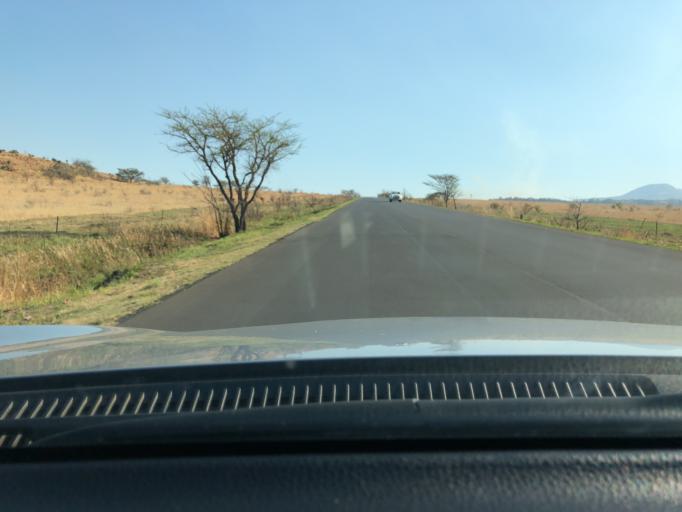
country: ZA
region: KwaZulu-Natal
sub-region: uThukela District Municipality
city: Ekuvukeni
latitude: -28.3646
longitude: 29.9999
